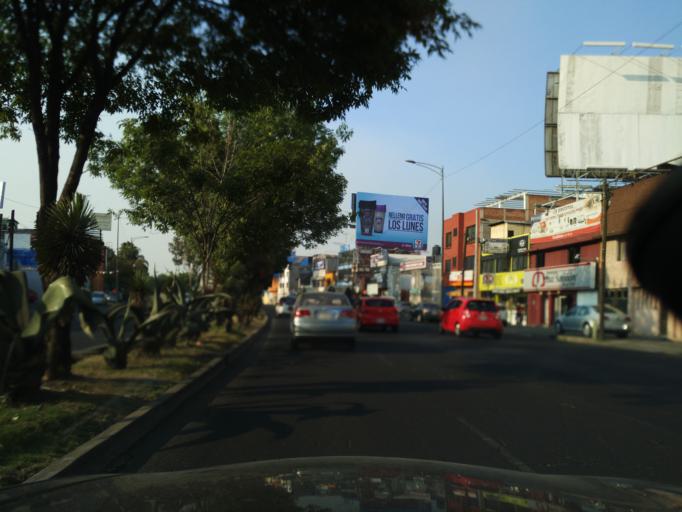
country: MX
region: Mexico City
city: Xochimilco
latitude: 19.3133
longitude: -99.1104
